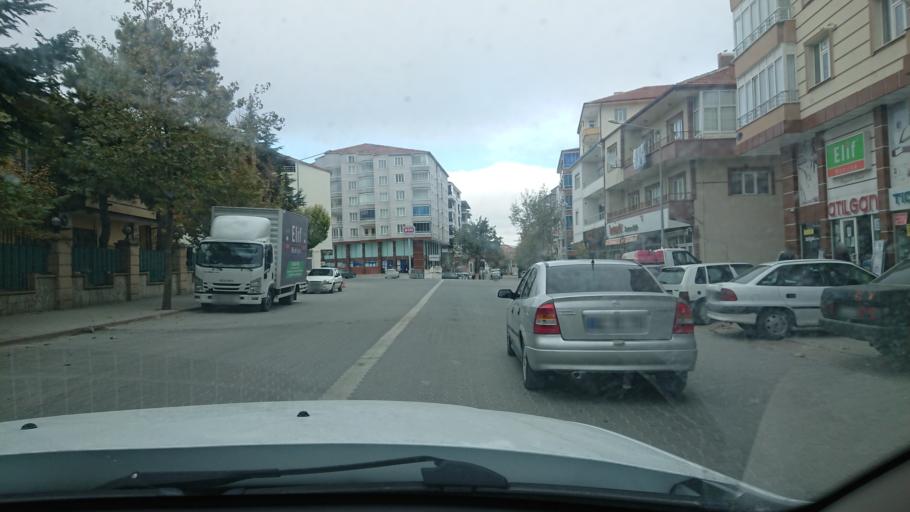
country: TR
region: Aksaray
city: Ortakoy
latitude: 38.7383
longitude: 34.0386
